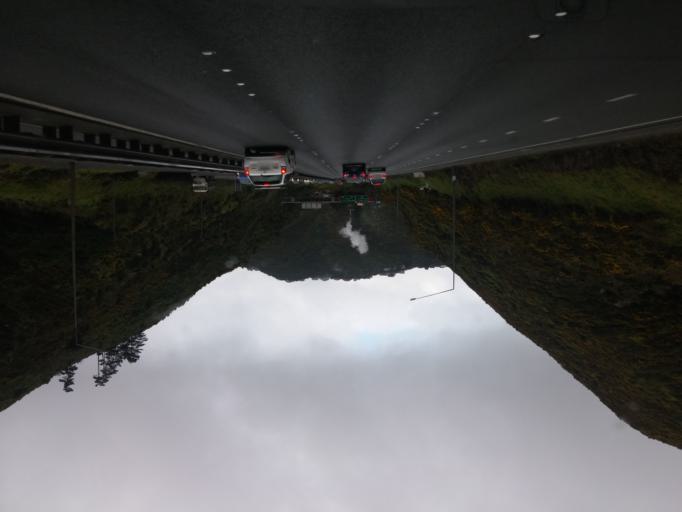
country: NZ
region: Wellington
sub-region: Wellington City
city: Wellington
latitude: -41.2335
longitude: 174.8078
